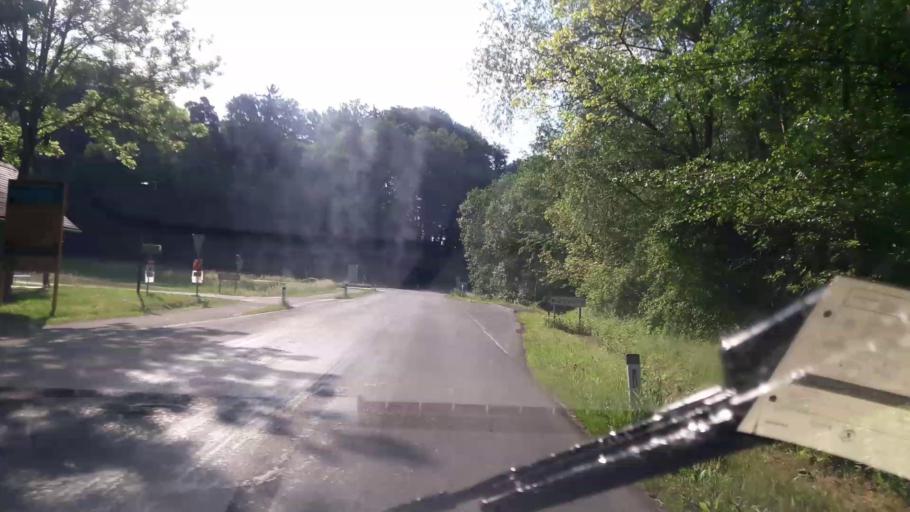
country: AT
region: Styria
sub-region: Politischer Bezirk Suedoststeiermark
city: Unterlamm
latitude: 46.9713
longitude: 16.0687
